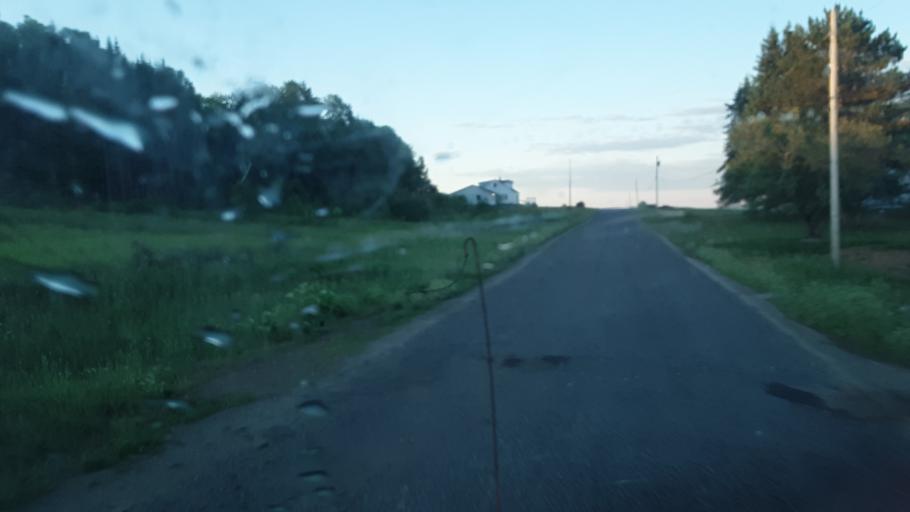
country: US
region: Maine
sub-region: Aroostook County
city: Caribou
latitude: 46.8114
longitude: -68.1352
